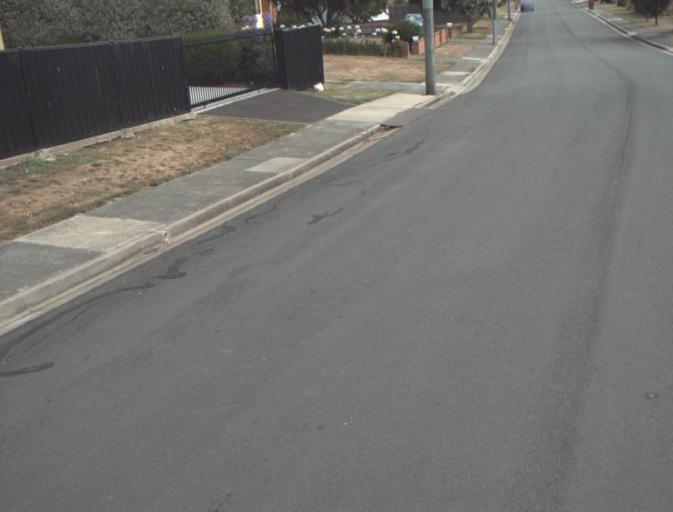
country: AU
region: Tasmania
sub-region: Launceston
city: Newstead
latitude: -41.4237
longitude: 147.1789
